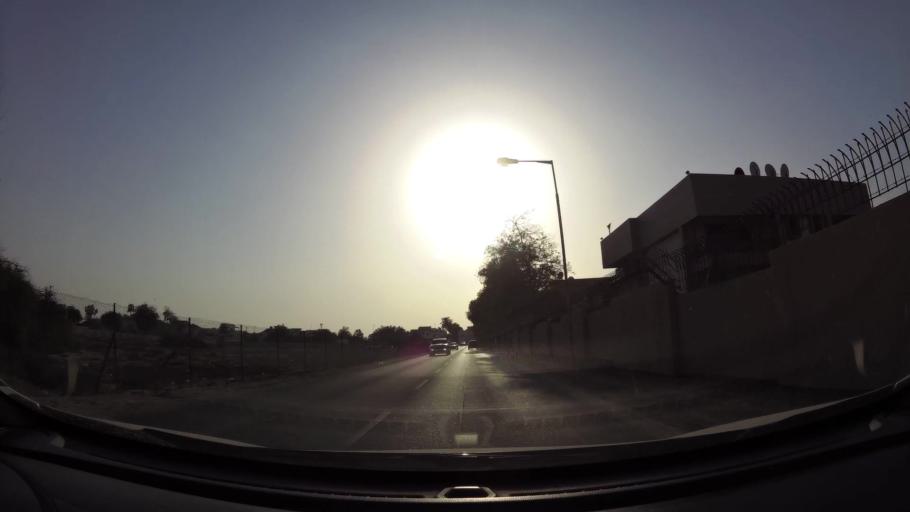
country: BH
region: Manama
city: Jidd Hafs
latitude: 26.2027
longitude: 50.4862
